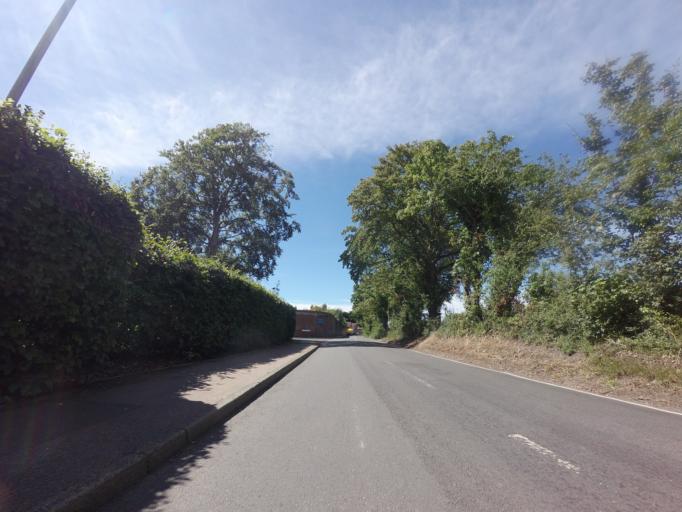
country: GB
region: England
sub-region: Kent
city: Sandwich
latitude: 51.2723
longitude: 1.3514
